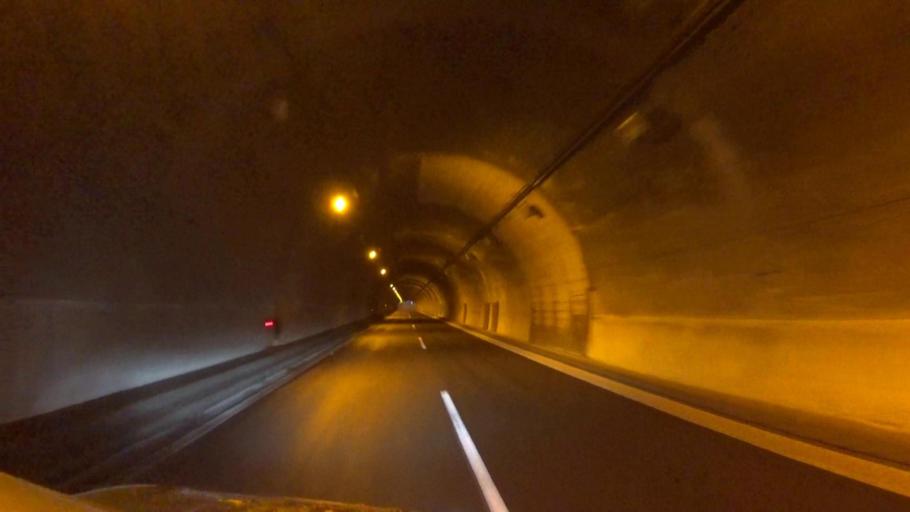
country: JP
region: Hokkaido
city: Otaru
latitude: 43.1696
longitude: 141.0415
